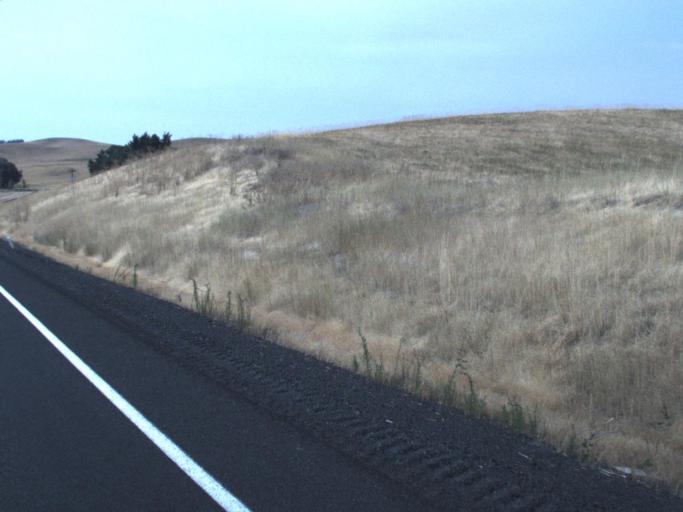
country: US
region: Washington
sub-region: Whitman County
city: Pullman
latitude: 46.7741
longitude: -117.1596
